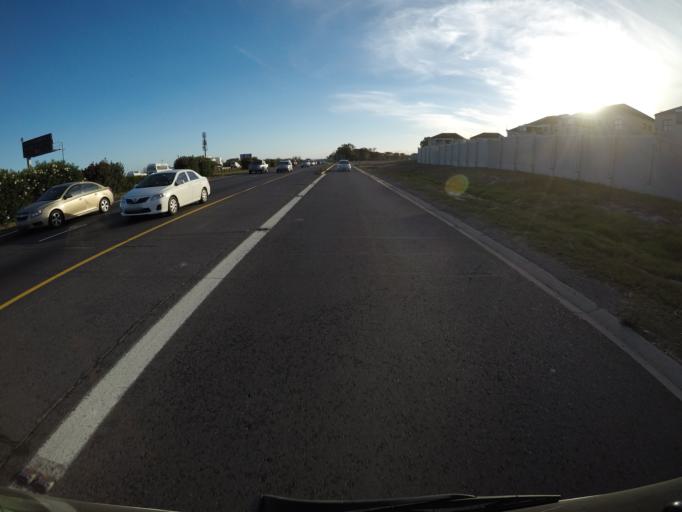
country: ZA
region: Western Cape
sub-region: City of Cape Town
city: Kraaifontein
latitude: -33.8633
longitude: 18.6869
